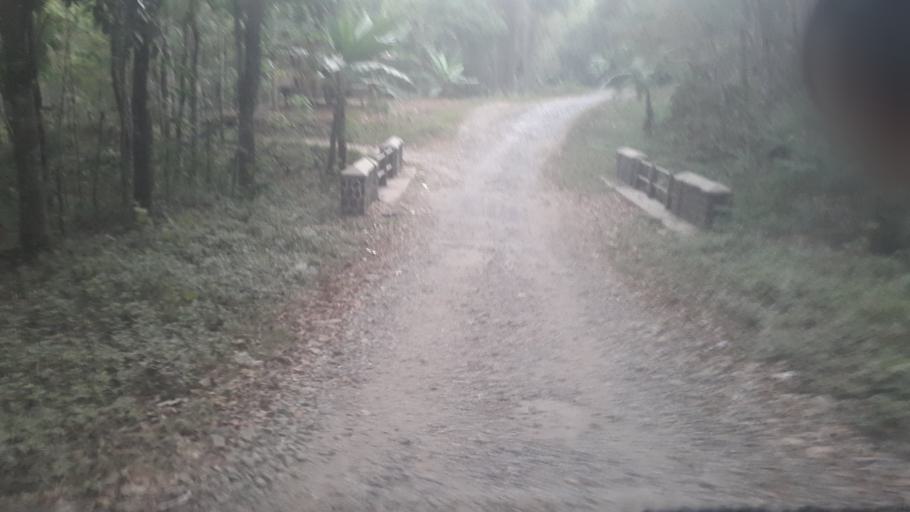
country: ID
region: West Java
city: Pelabuhanratu
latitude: -6.9423
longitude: 106.5952
